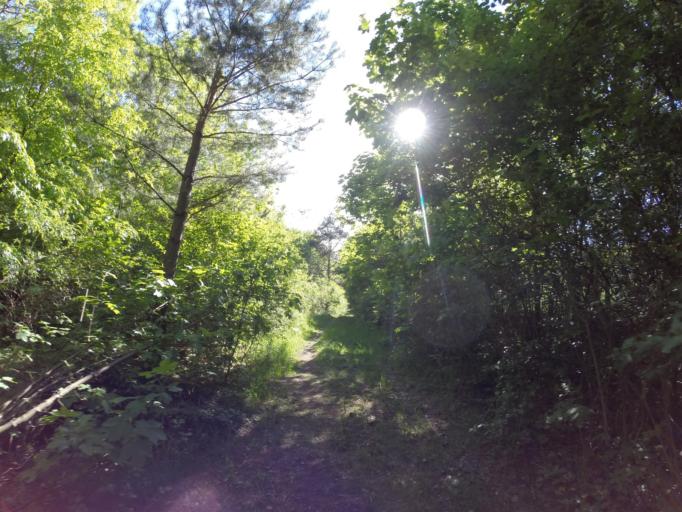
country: DE
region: Thuringia
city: Neuengonna
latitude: 50.9786
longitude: 11.6338
